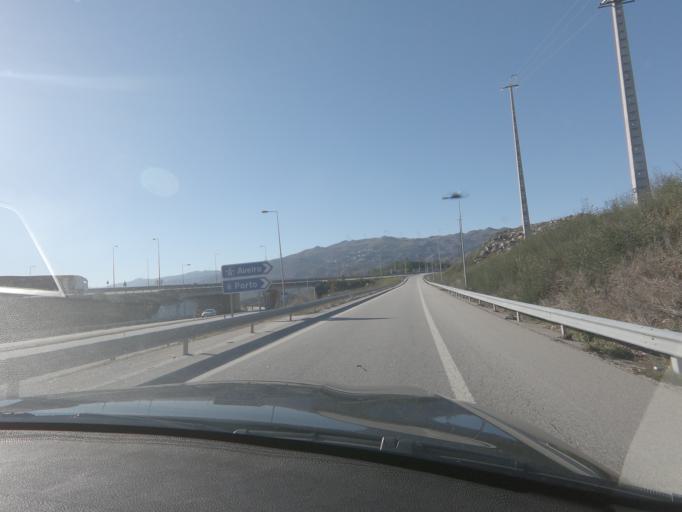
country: PT
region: Viseu
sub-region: Vouzela
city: Vouzela
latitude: 40.6458
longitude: -8.0604
